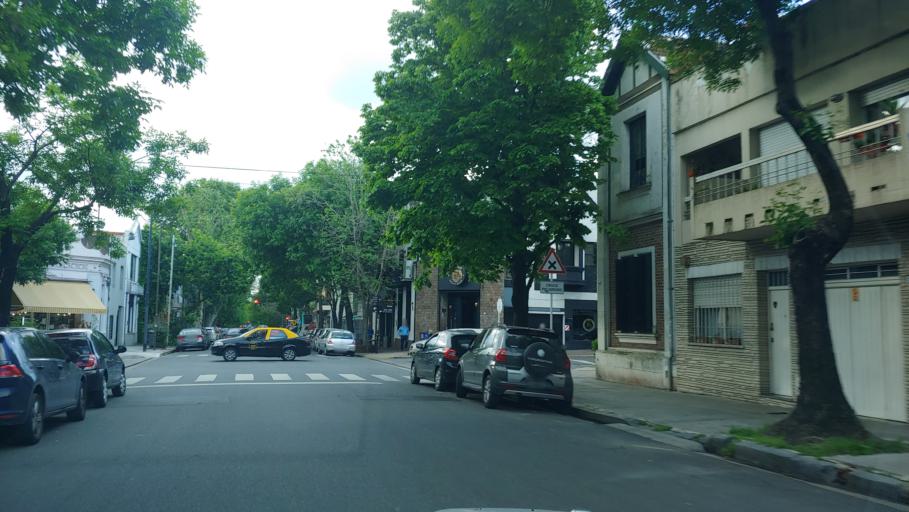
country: AR
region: Buenos Aires F.D.
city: Colegiales
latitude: -34.5747
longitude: -58.4539
